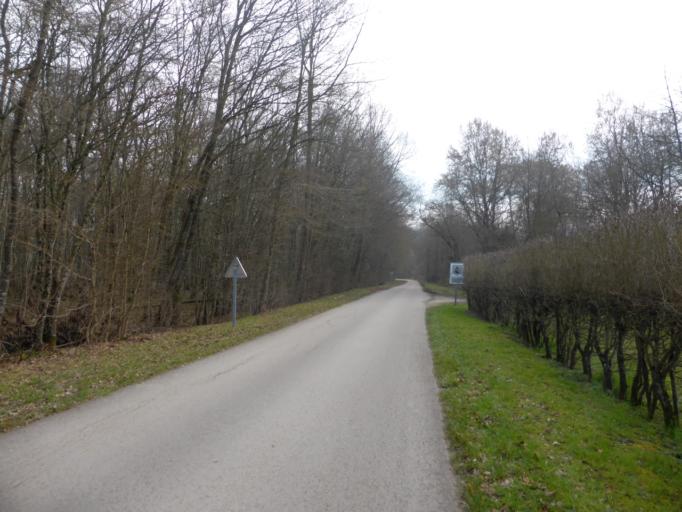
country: FR
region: Champagne-Ardenne
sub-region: Departement de l'Aube
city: Lusigny-sur-Barse
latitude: 48.2836
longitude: 4.3075
